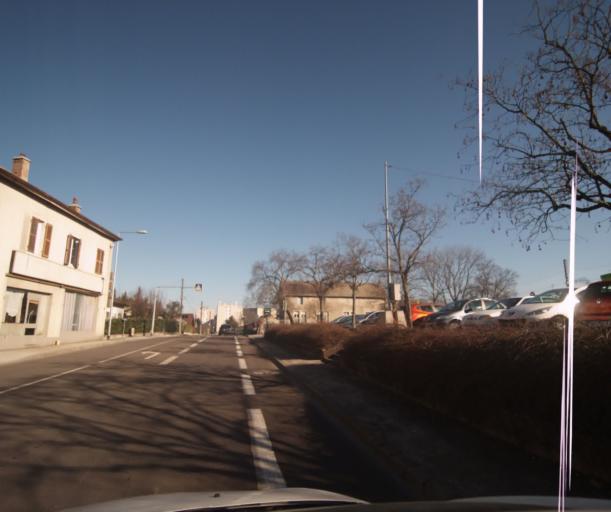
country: FR
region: Franche-Comte
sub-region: Departement du Doubs
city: Beure
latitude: 47.2309
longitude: 5.9929
